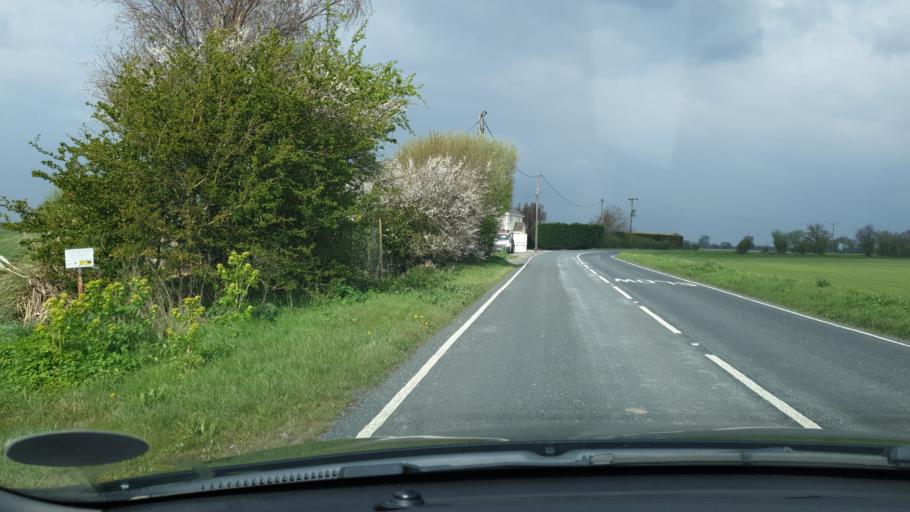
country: GB
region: England
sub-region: Essex
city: Mistley
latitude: 51.9181
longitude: 1.0856
